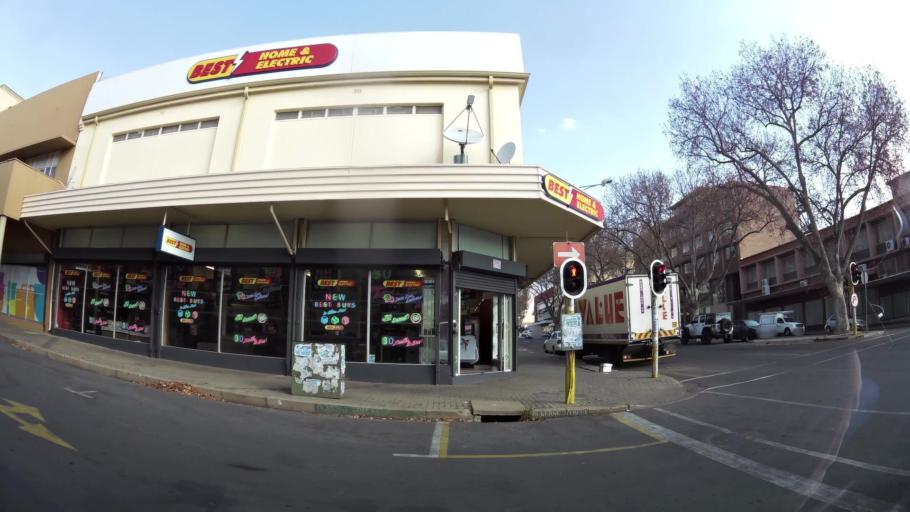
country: ZA
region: Gauteng
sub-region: West Rand District Municipality
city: Krugersdorp
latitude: -26.1022
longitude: 27.7709
